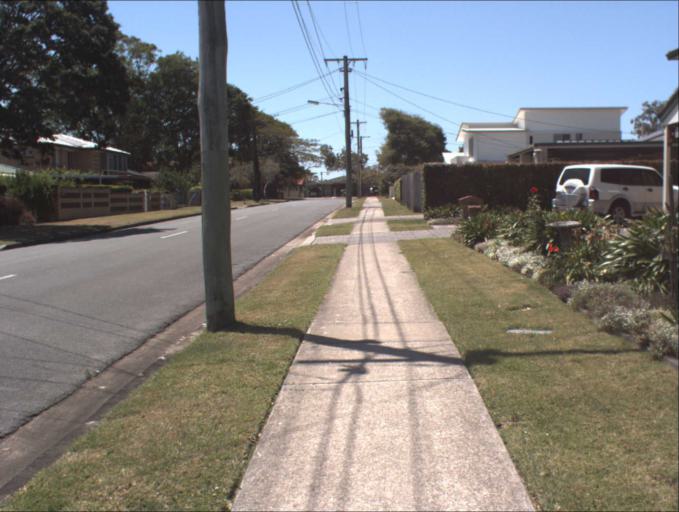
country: AU
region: Queensland
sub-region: Logan
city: Rochedale South
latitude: -27.5930
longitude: 153.1252
